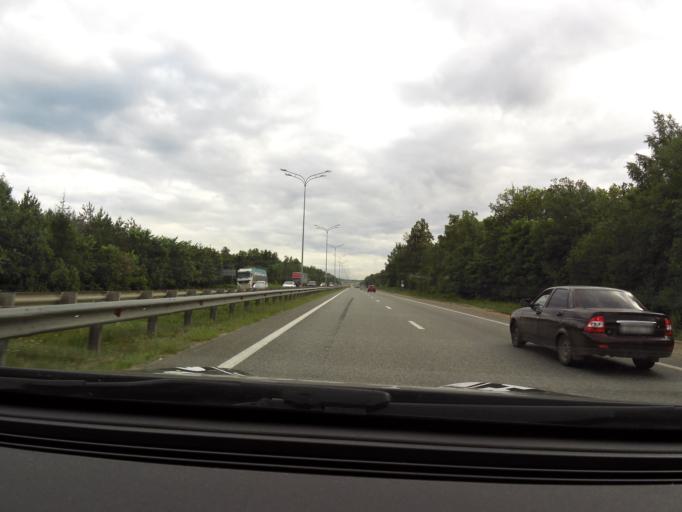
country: RU
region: Tatarstan
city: Sviyazhsk
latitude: 55.7501
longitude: 48.8000
